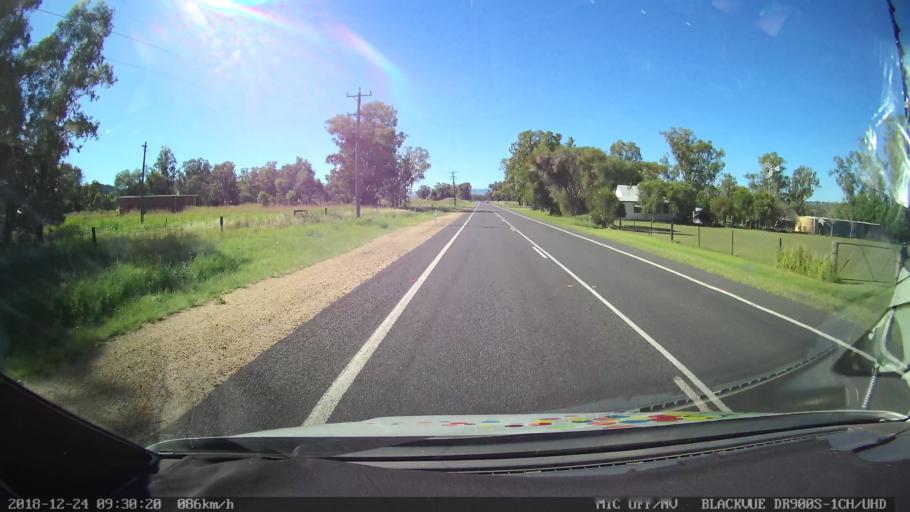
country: AU
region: New South Wales
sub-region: Liverpool Plains
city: Quirindi
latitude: -31.5610
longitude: 150.6971
